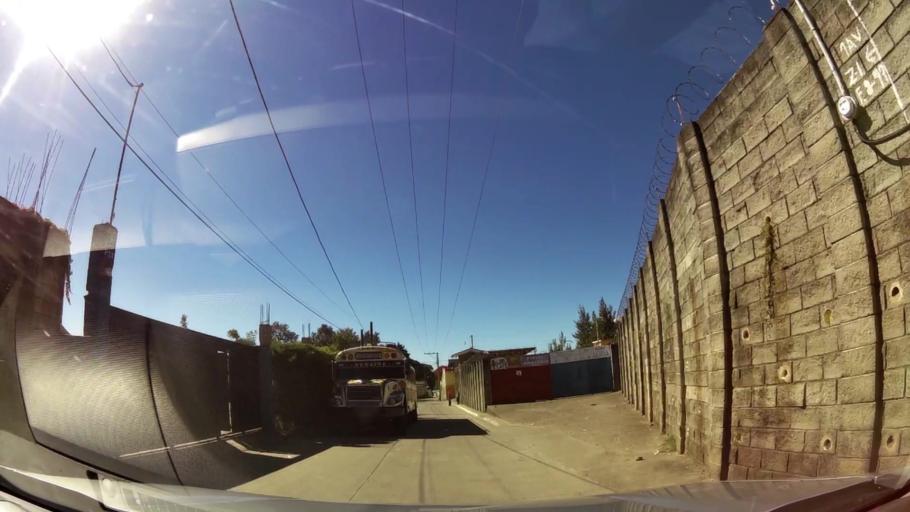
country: GT
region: Guatemala
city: Fraijanes
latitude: 14.4567
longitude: -90.4421
